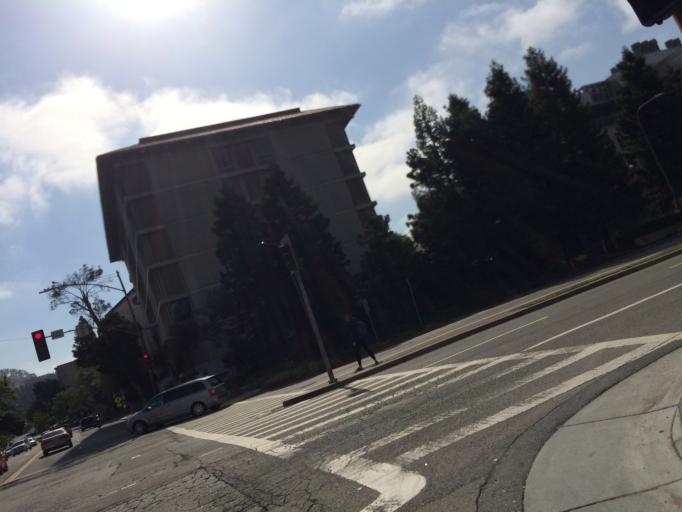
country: US
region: California
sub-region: Alameda County
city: Berkeley
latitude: 37.8741
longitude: -122.2665
